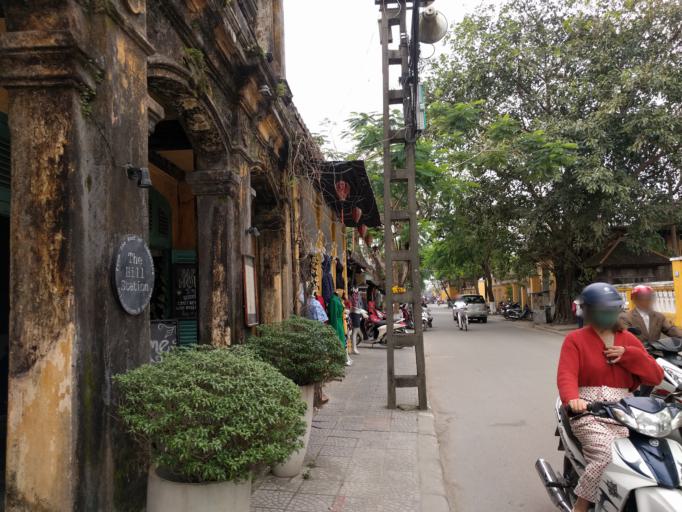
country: VN
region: Quang Nam
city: Hoi An
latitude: 15.8779
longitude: 108.3340
